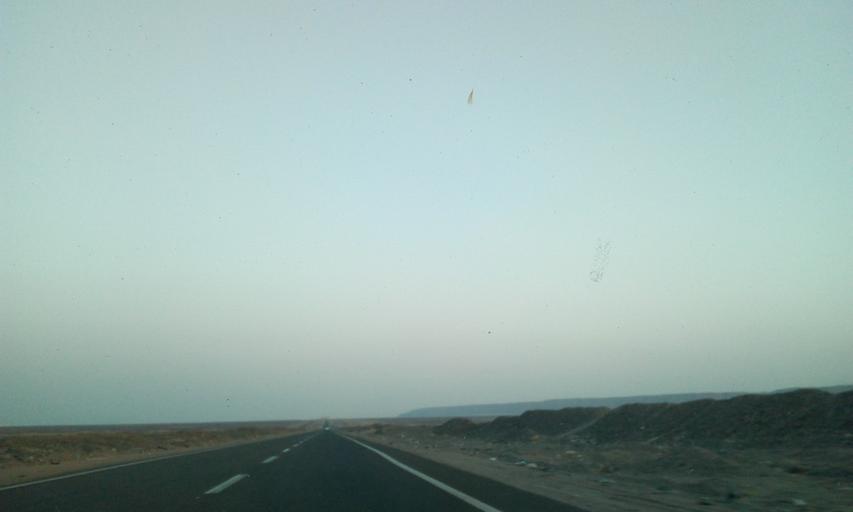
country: EG
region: Red Sea
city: El Gouna
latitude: 27.4685
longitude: 33.5867
